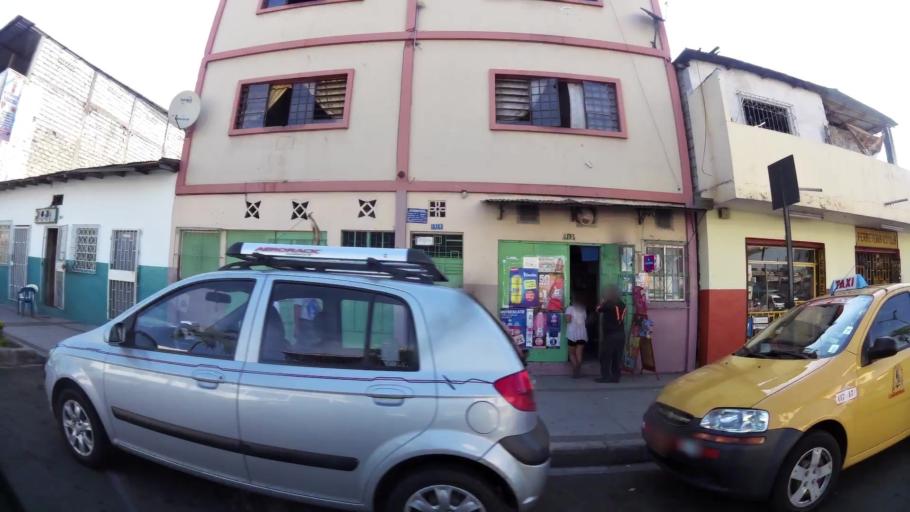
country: EC
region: Guayas
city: Guayaquil
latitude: -2.1991
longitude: -79.9154
